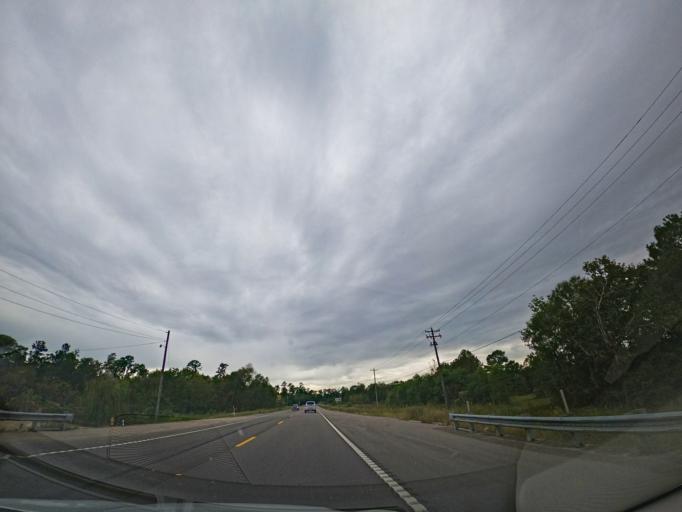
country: US
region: Mississippi
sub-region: Hancock County
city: Pearlington
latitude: 30.2422
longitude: -89.6059
